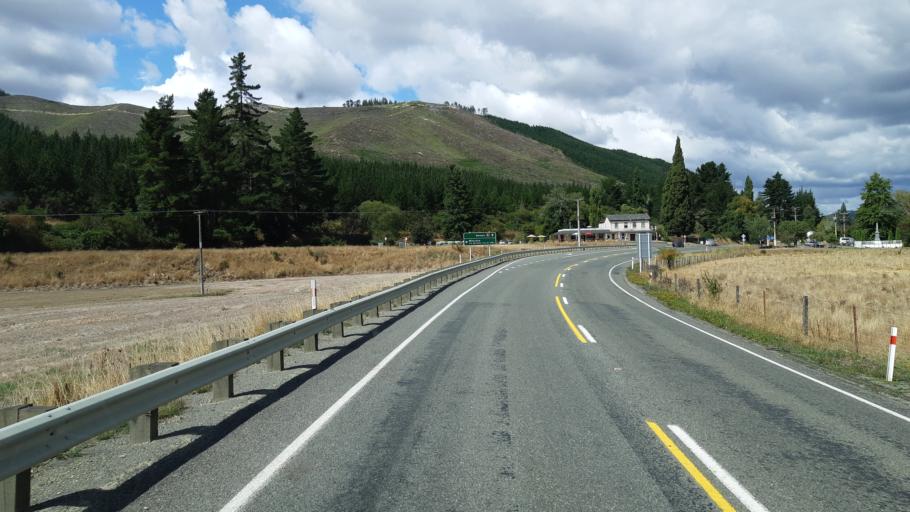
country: NZ
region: Tasman
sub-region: Tasman District
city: Wakefield
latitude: -41.4498
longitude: 172.8352
